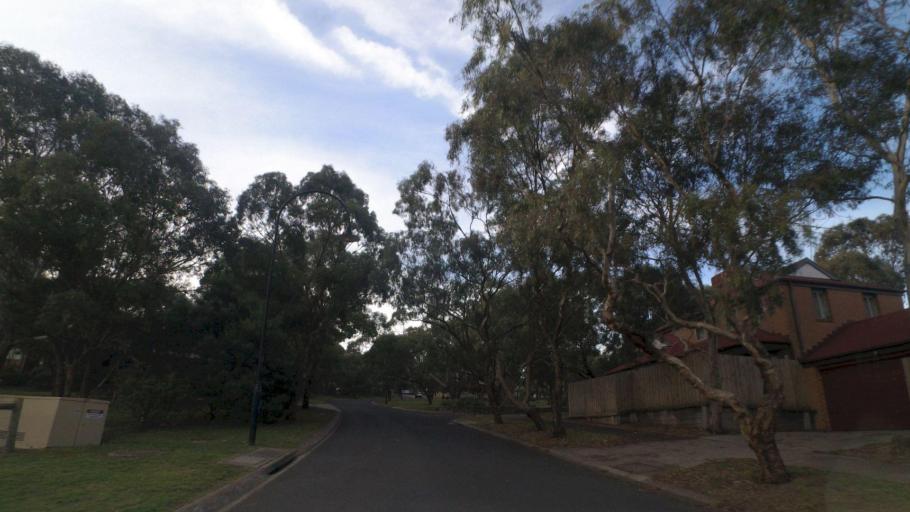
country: AU
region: Victoria
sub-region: Banyule
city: Yallambie
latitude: -37.7232
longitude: 145.1005
